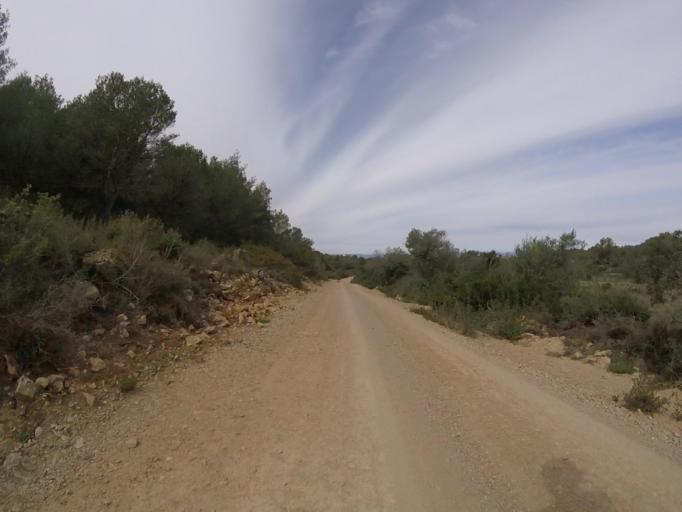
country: ES
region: Valencia
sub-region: Provincia de Castello
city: Cabanes
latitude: 40.1949
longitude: 0.0790
